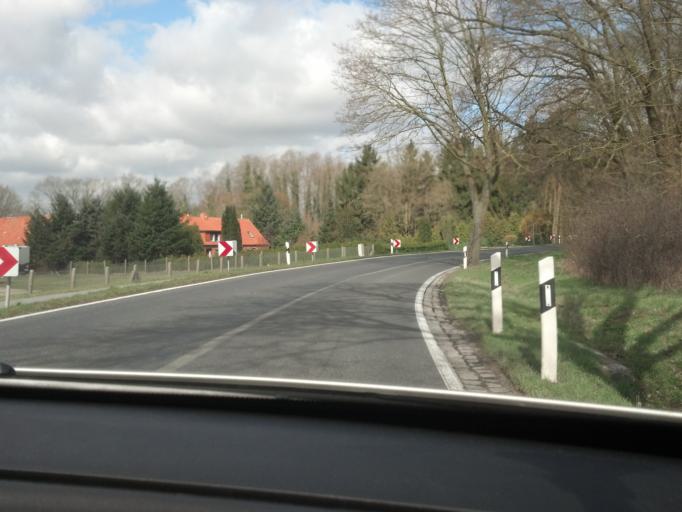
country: DE
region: Mecklenburg-Vorpommern
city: Boizenburg
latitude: 53.4083
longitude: 10.7417
